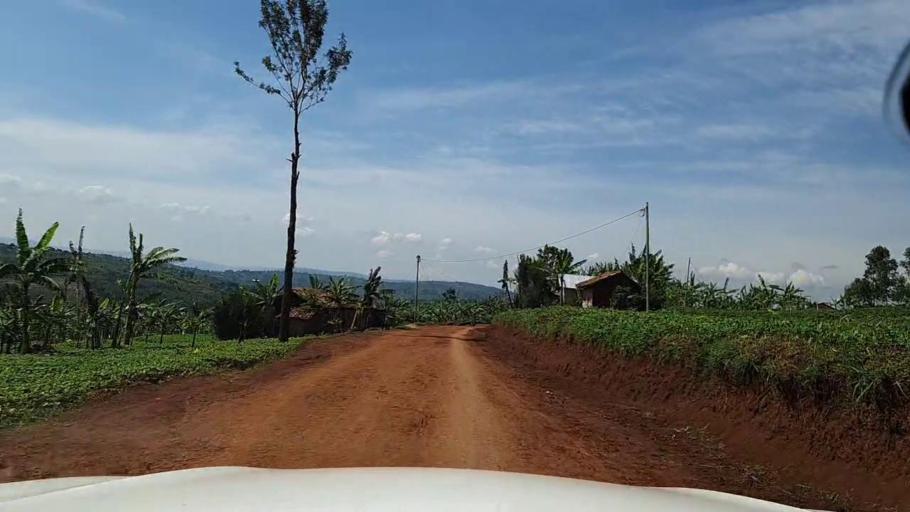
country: RW
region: Southern Province
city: Butare
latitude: -2.7040
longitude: 29.8454
